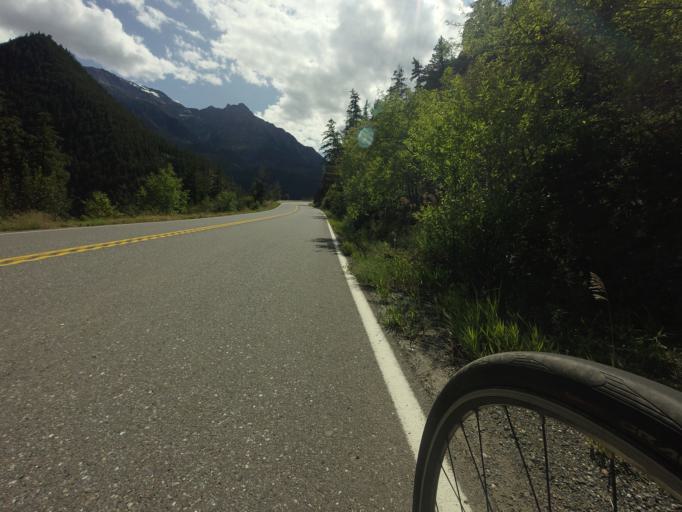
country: CA
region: British Columbia
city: Lillooet
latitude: 50.6595
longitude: -121.9925
